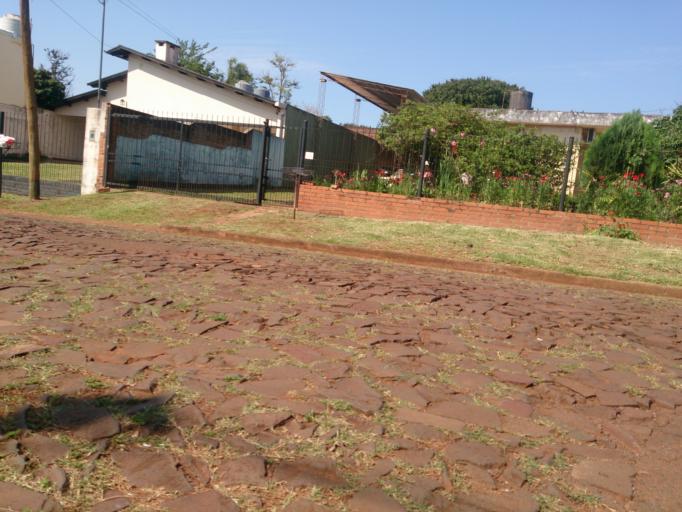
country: AR
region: Misiones
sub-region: Departamento de Obera
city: Obera
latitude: -27.4870
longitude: -55.1075
